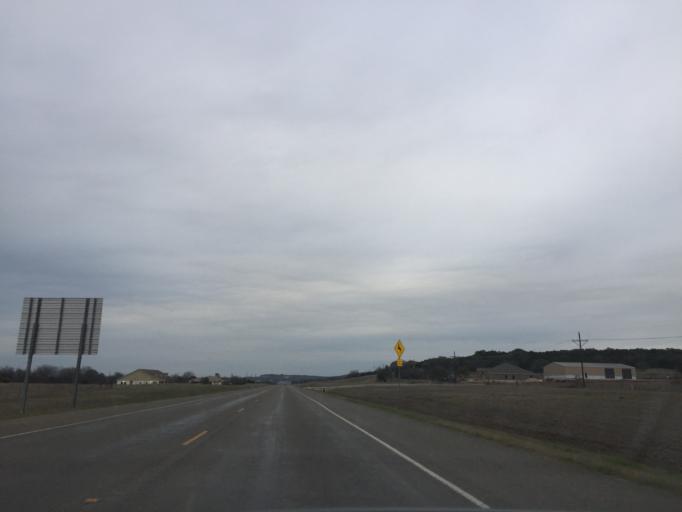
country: US
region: Texas
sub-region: Coryell County
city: Gatesville
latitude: 31.4494
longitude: -97.7151
